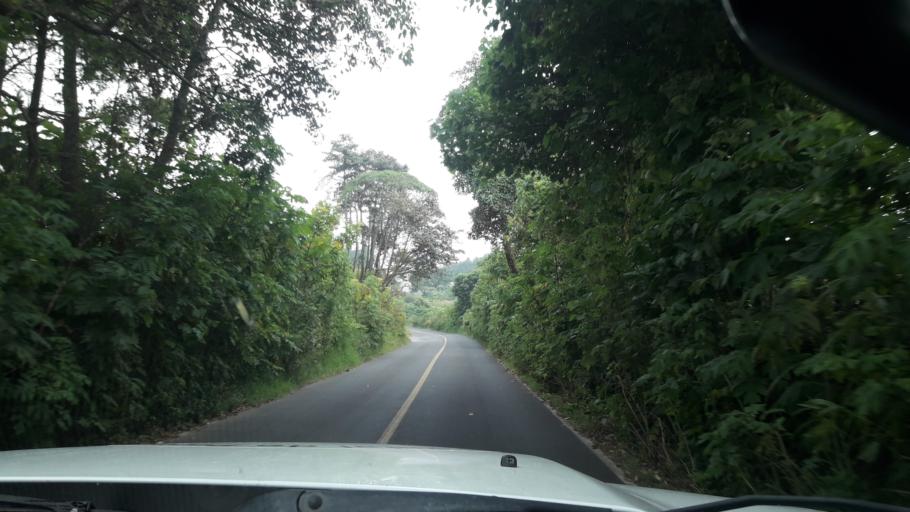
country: MX
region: Colima
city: Suchitlan
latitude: 19.4119
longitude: -103.6468
